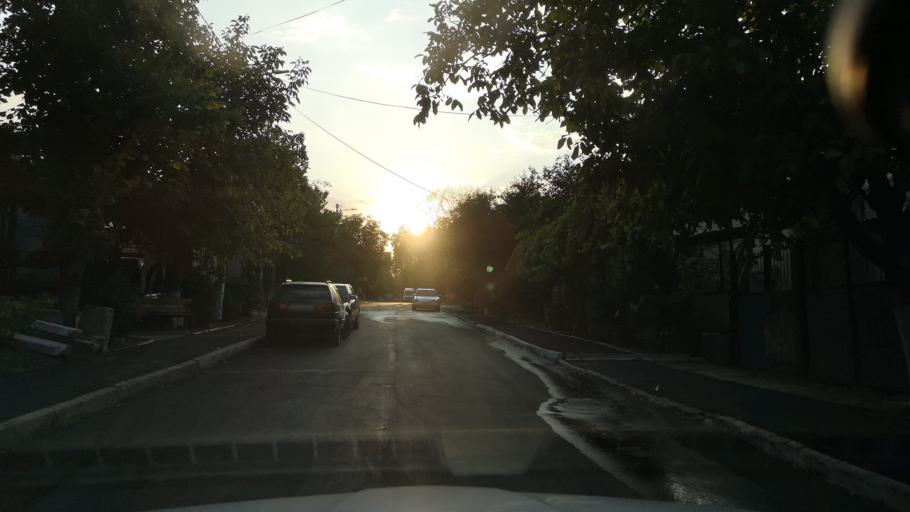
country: MD
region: Rezina
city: Rezina
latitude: 47.7531
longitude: 28.9585
